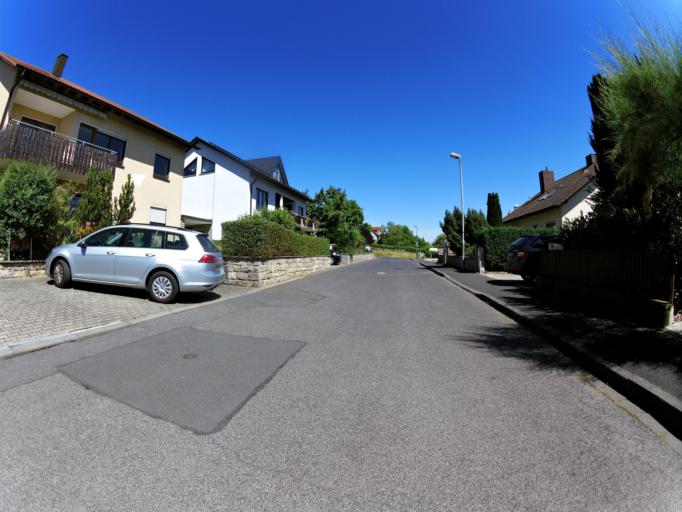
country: DE
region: Bavaria
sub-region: Regierungsbezirk Unterfranken
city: Ochsenfurt
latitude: 49.6726
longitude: 10.0571
